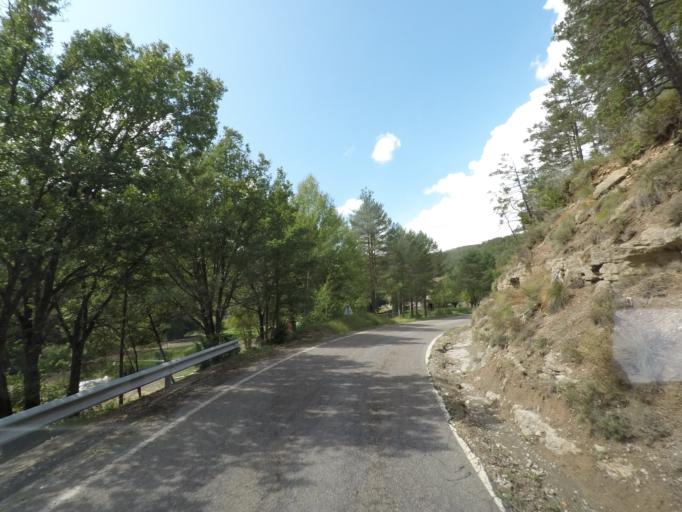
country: ES
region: Aragon
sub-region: Provincia de Huesca
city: Yebra de Basa
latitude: 42.4077
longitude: -0.1979
